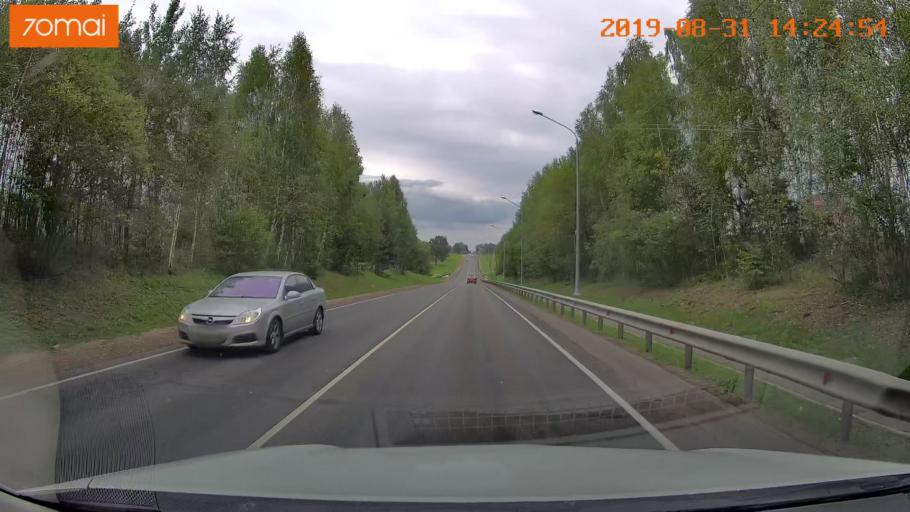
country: RU
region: Smolensk
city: Yekimovichi
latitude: 54.1055
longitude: 33.2638
